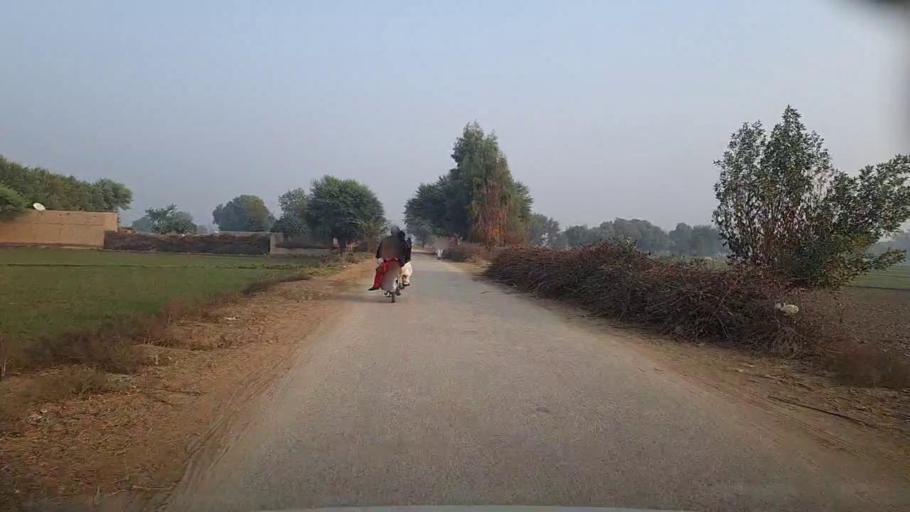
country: PK
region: Sindh
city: Bozdar
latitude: 27.0817
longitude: 68.5697
